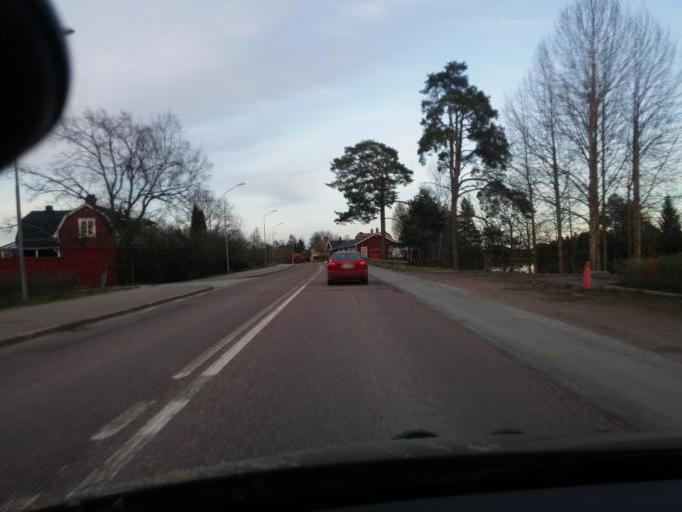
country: SE
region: Gaevleborg
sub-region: Ljusdals Kommun
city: Ljusdal
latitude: 61.8385
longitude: 16.0514
